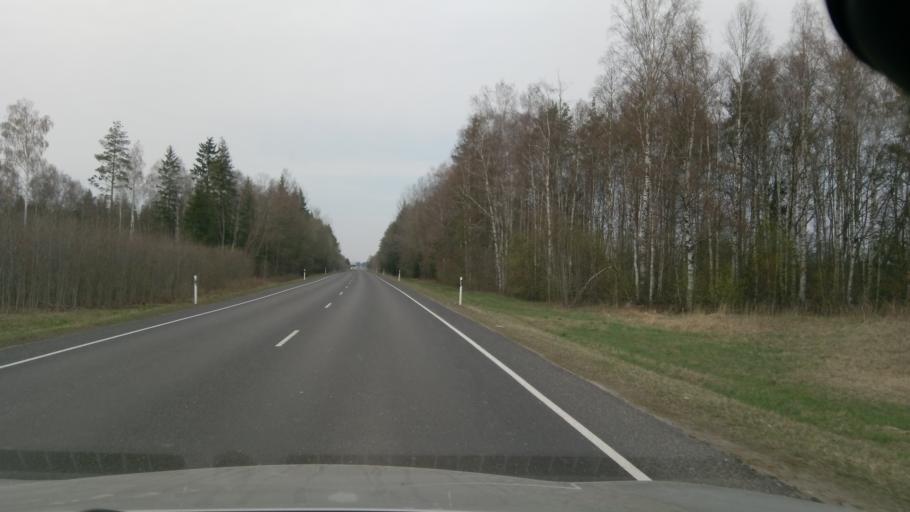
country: EE
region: Viljandimaa
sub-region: Vohma linn
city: Vohma
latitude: 58.7387
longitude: 25.5851
